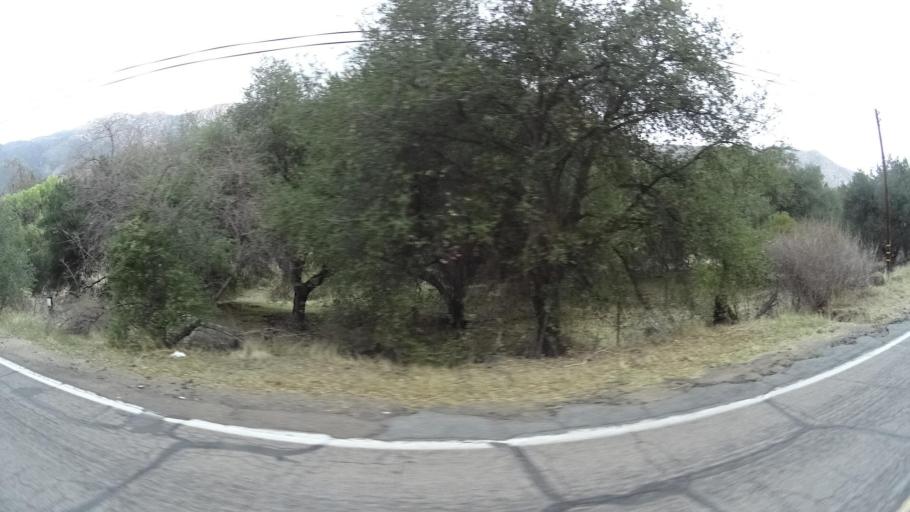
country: US
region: California
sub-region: San Diego County
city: Harbison Canyon
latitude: 32.8880
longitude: -116.8354
